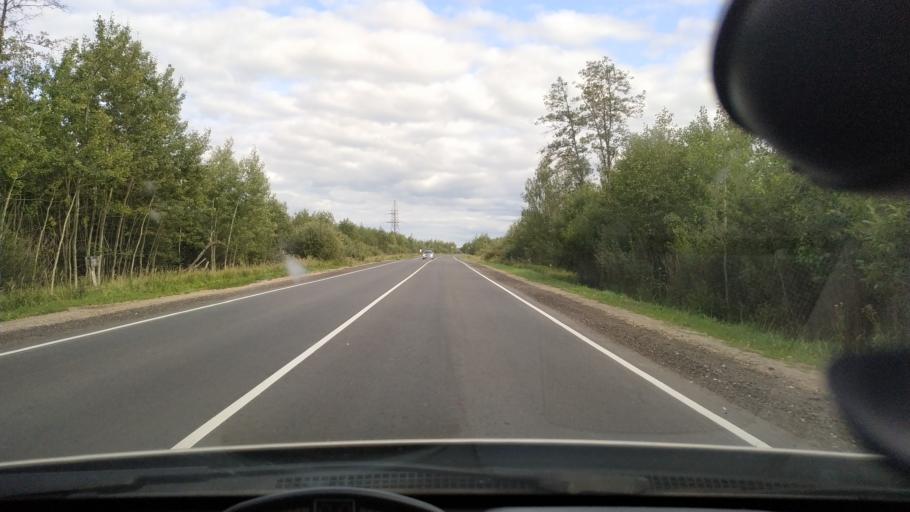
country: RU
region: Moskovskaya
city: Vereya
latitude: 55.7258
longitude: 39.0431
